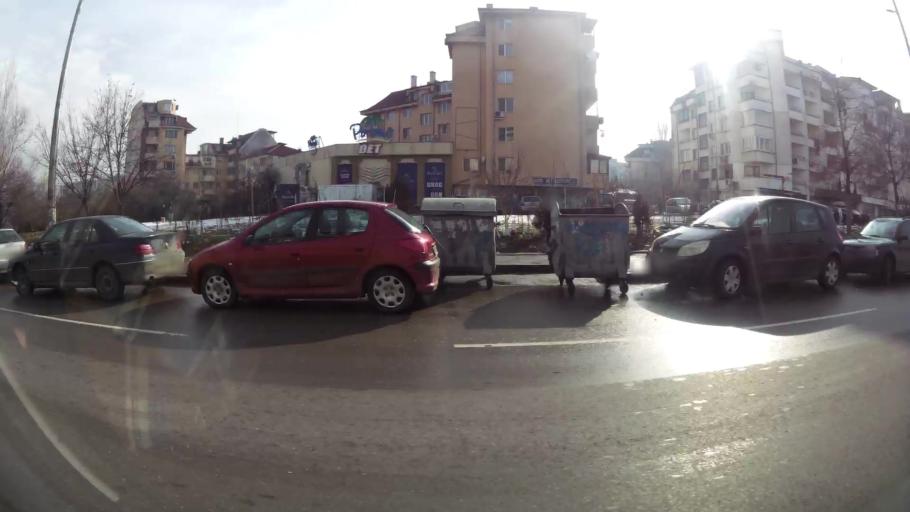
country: BG
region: Sofiya
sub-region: Obshtina Bozhurishte
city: Bozhurishte
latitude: 42.7229
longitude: 23.2581
